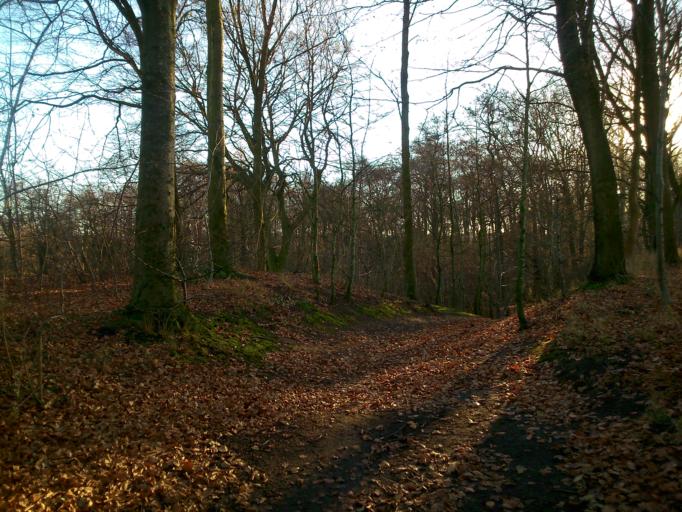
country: DK
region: Central Jutland
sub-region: Holstebro Kommune
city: Holstebro
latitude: 56.3634
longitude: 8.6302
